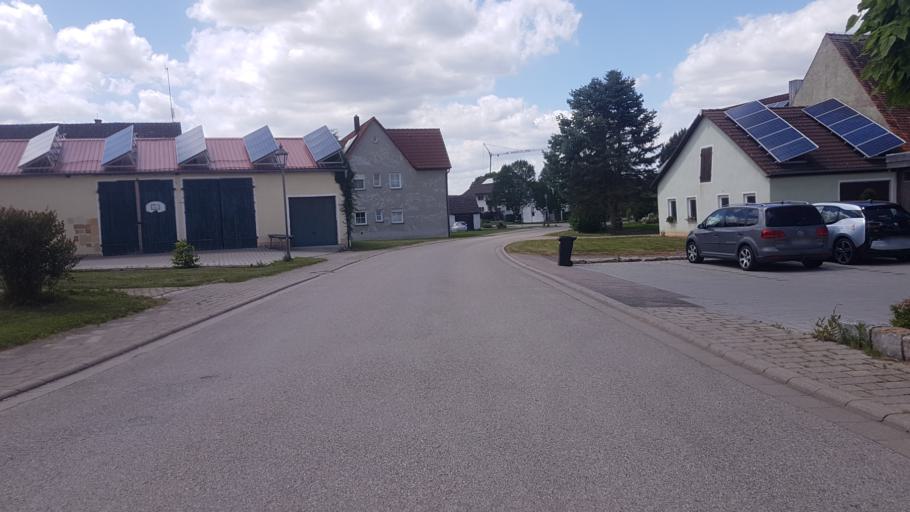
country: DE
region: Bavaria
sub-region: Regierungsbezirk Mittelfranken
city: Geslau
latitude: 49.3469
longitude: 10.3295
